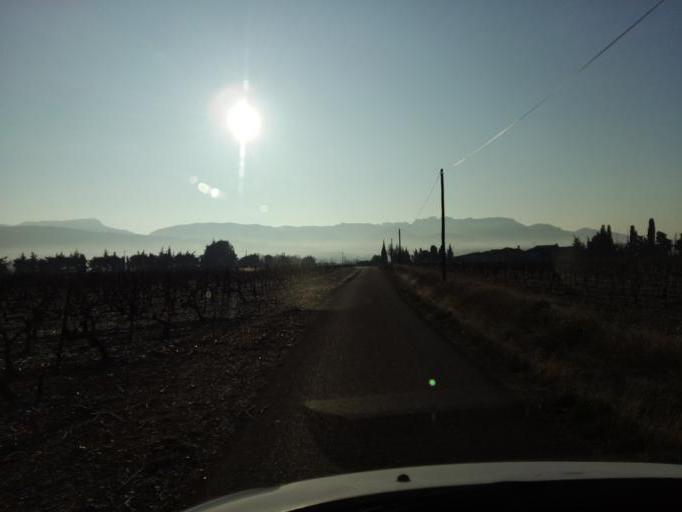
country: FR
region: Provence-Alpes-Cote d'Azur
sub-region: Departement du Vaucluse
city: Sablet
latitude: 44.2039
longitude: 4.9803
